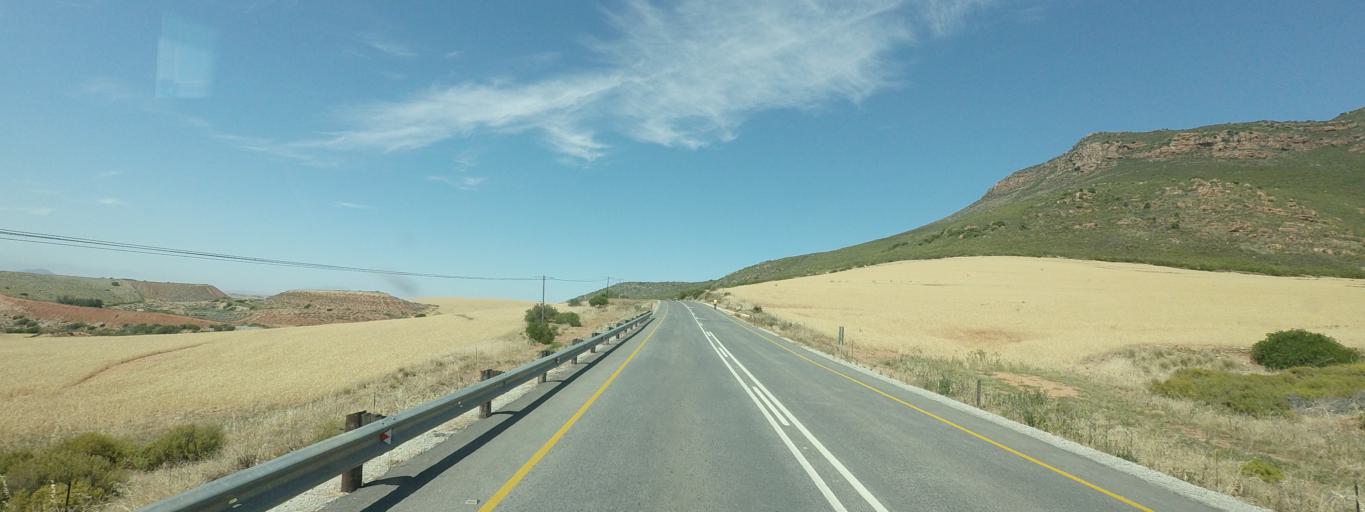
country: ZA
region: Western Cape
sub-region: West Coast District Municipality
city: Piketberg
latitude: -32.9225
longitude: 18.7574
